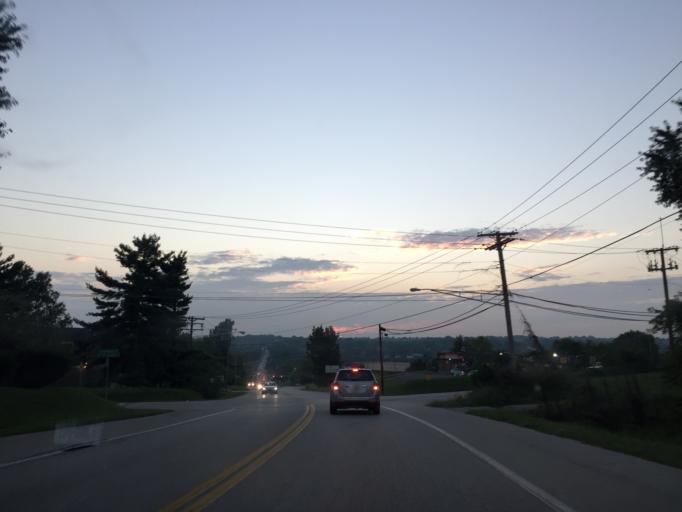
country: US
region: Maryland
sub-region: Baltimore County
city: Rosedale
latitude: 39.3318
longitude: -76.5254
